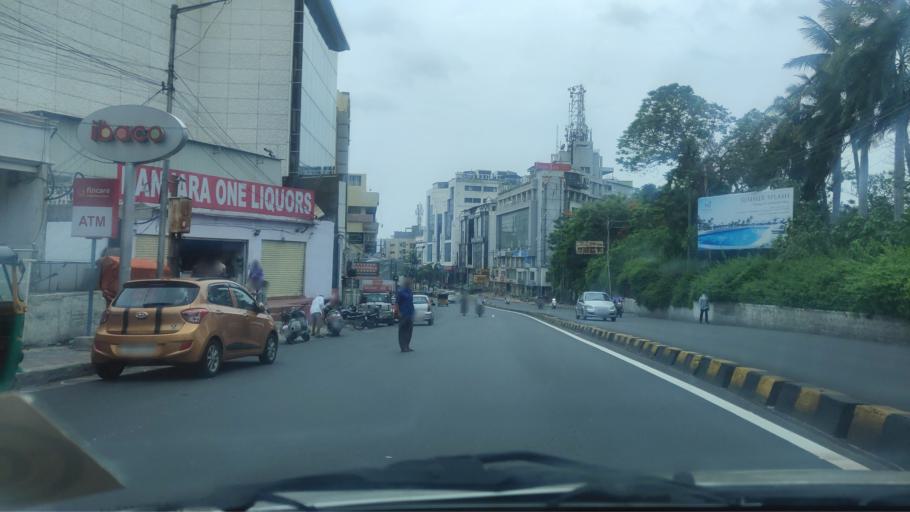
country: IN
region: Telangana
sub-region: Hyderabad
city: Hyderabad
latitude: 17.4111
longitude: 78.4497
